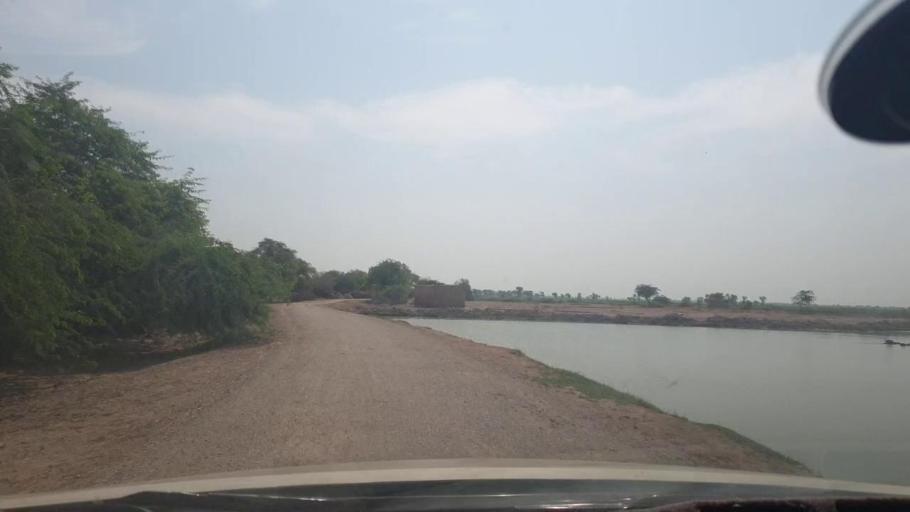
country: PK
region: Sindh
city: Jacobabad
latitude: 28.2735
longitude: 68.5262
